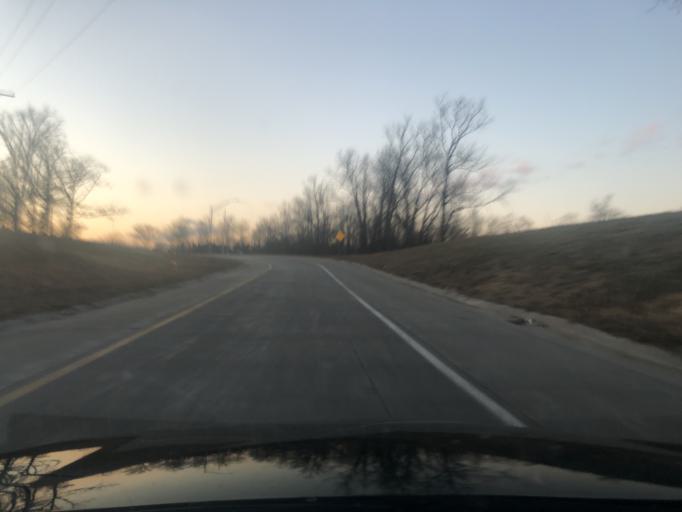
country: US
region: Michigan
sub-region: Wayne County
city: Taylor
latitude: 42.2544
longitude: -83.3002
